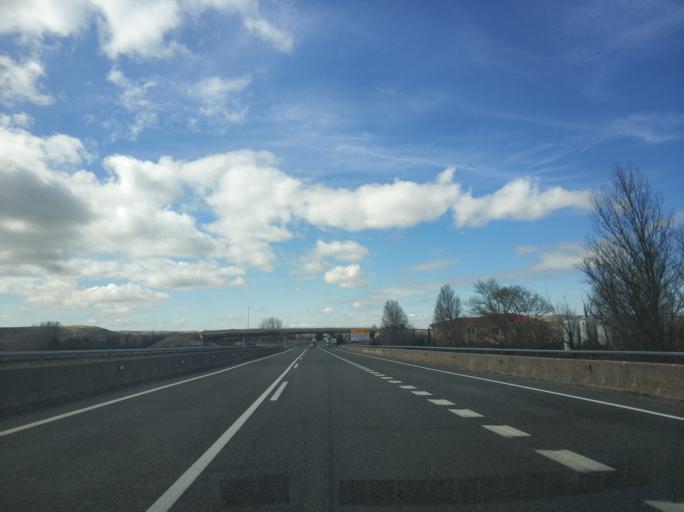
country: ES
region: Castille and Leon
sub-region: Provincia de Burgos
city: Frandovinez
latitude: 42.3014
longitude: -3.8334
